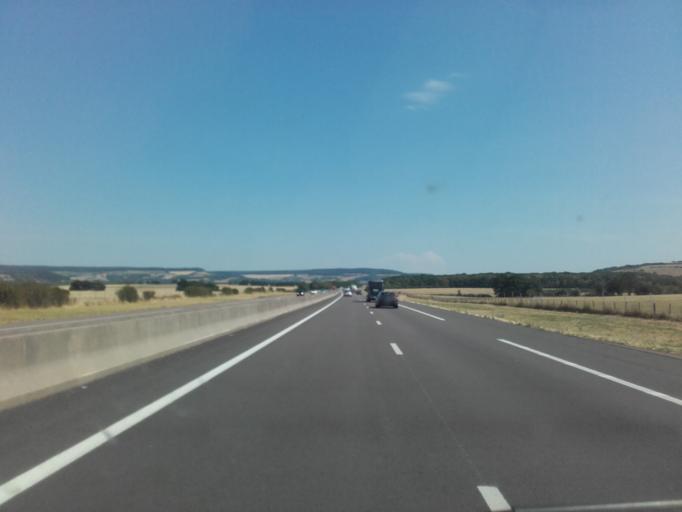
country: FR
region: Bourgogne
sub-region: Departement de la Cote-d'Or
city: Vitteaux
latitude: 47.3564
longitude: 4.4344
